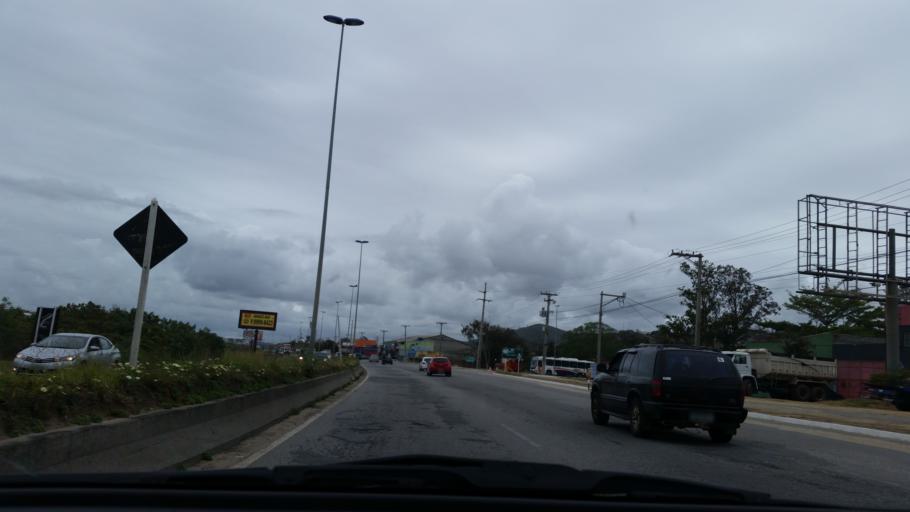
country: BR
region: Rio de Janeiro
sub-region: Sao Pedro Da Aldeia
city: Sao Pedro da Aldeia
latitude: -22.8494
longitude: -42.0636
